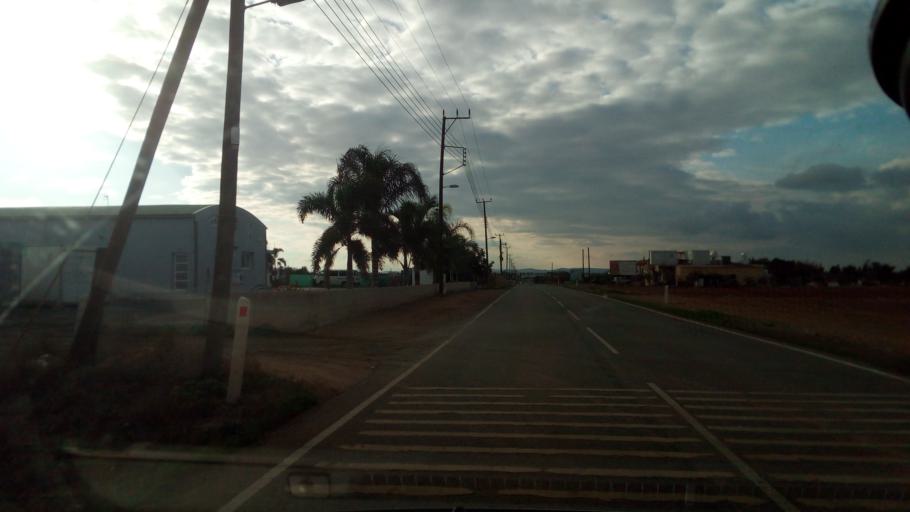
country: CY
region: Ammochostos
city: Avgorou
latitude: 35.0411
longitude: 33.8613
